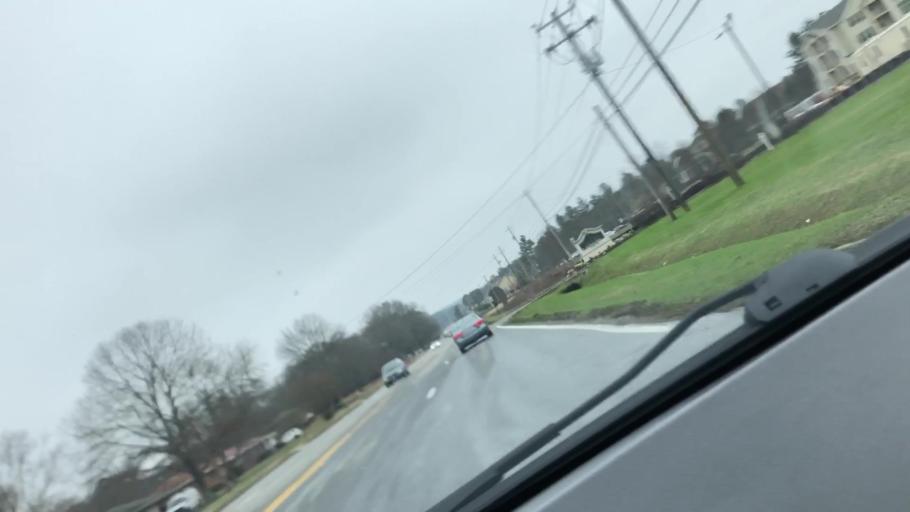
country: US
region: Georgia
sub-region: Bartow County
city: Cartersville
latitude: 34.2119
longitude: -84.8190
